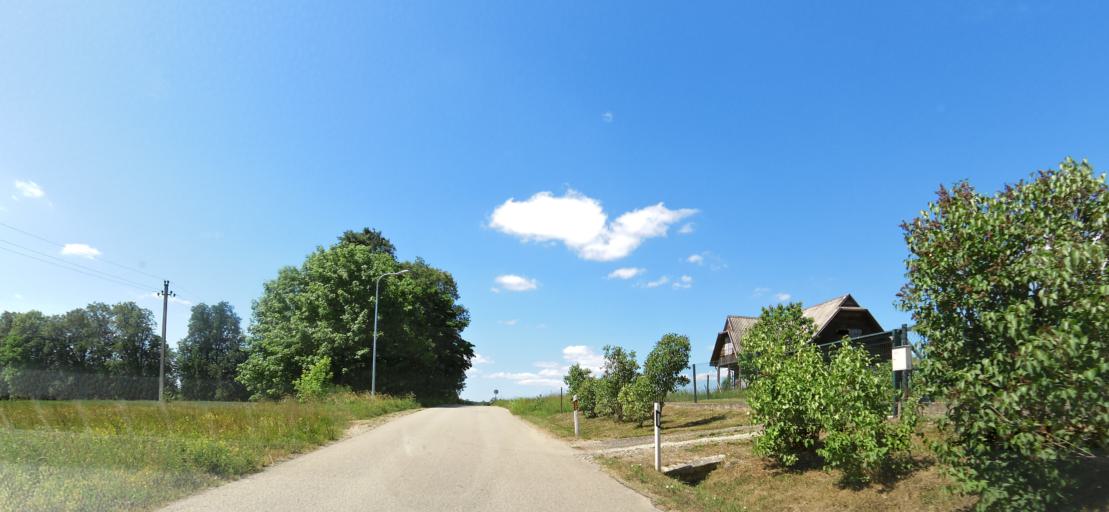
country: LT
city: Nemencine
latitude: 54.8758
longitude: 25.5403
